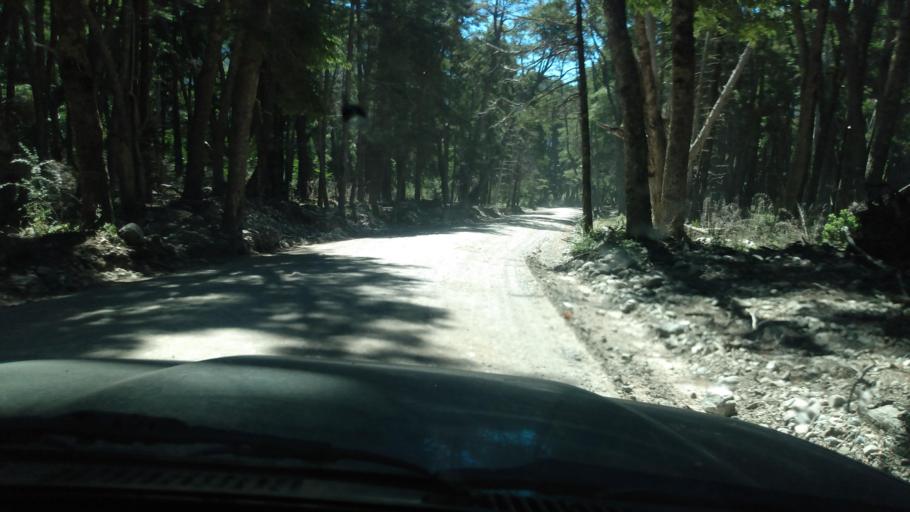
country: AR
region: Neuquen
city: Villa La Angostura
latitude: -40.6235
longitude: -71.5939
